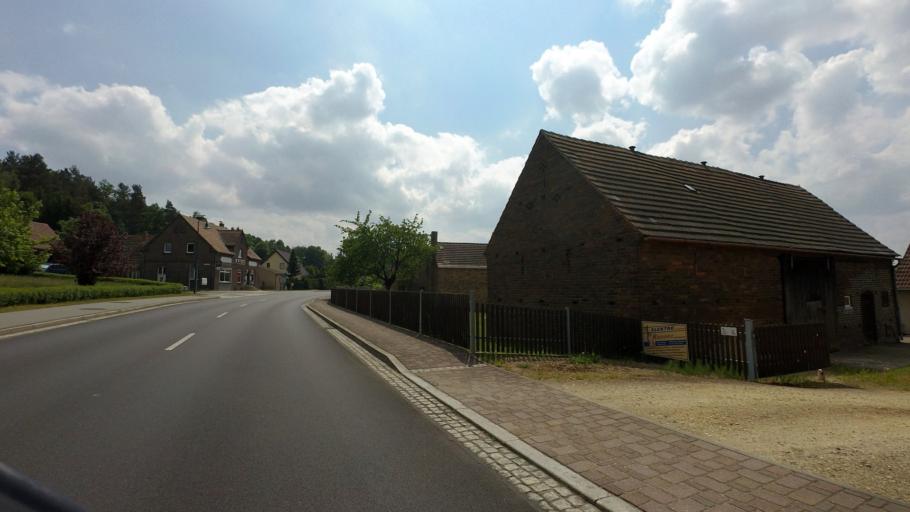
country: DE
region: Saxony
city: Rietschen
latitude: 51.3572
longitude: 14.8028
